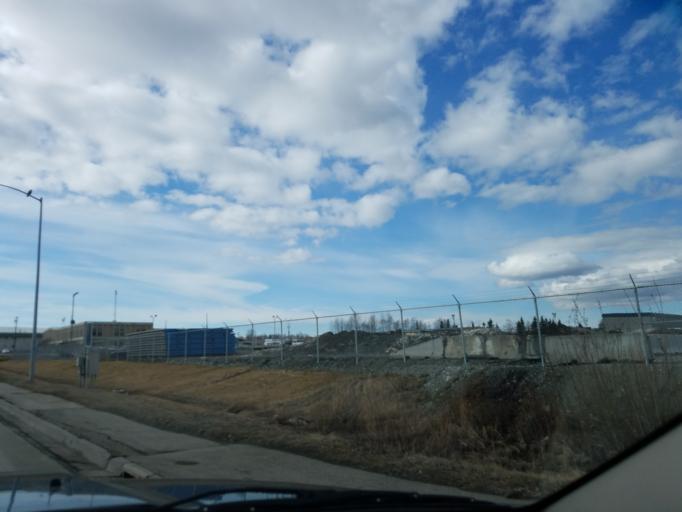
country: US
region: Alaska
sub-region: Anchorage Municipality
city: Anchorage
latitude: 61.1736
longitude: -149.8731
